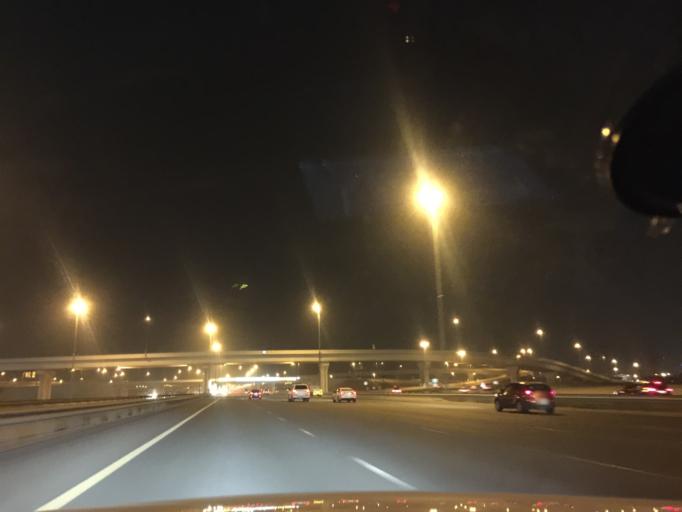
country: AE
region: Dubai
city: Dubai
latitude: 25.1053
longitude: 55.2357
